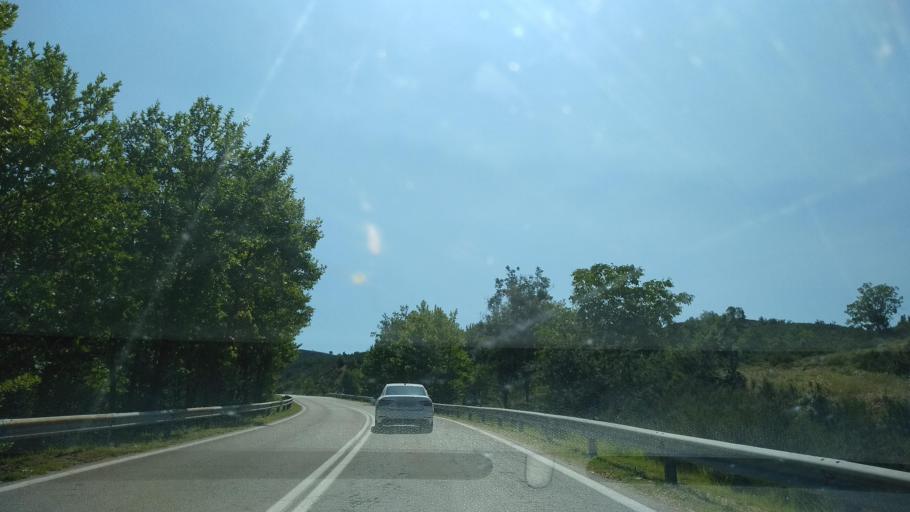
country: GR
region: Central Macedonia
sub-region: Nomos Chalkidikis
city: Arnaia
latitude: 40.4998
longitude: 23.4943
